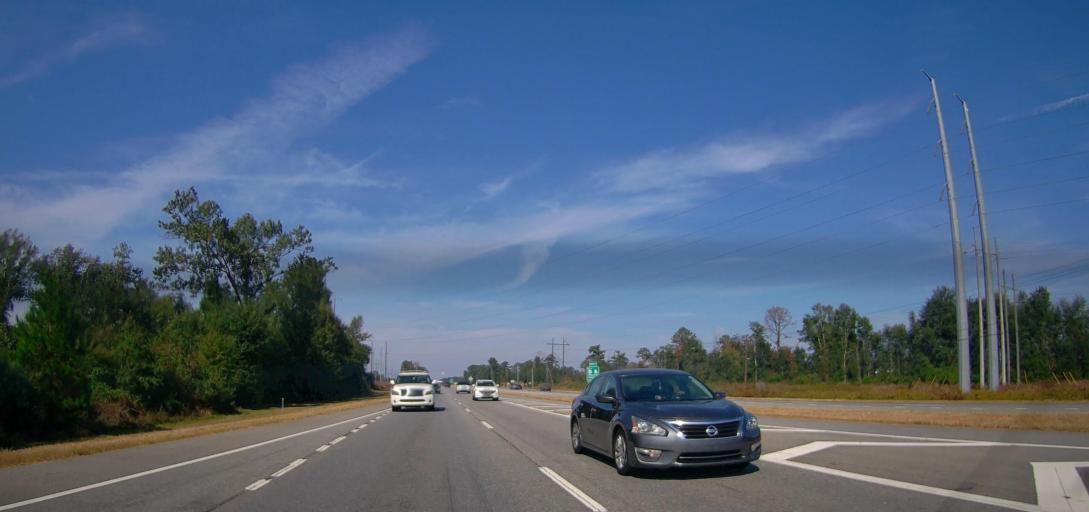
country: US
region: Georgia
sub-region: Dougherty County
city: Putney
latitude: 31.5309
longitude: -84.1156
